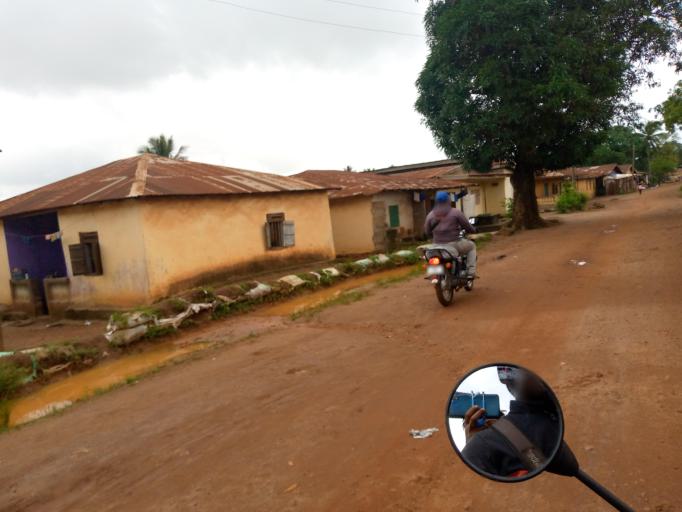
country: SL
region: Eastern Province
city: Kenema
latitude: 7.8662
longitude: -11.1937
